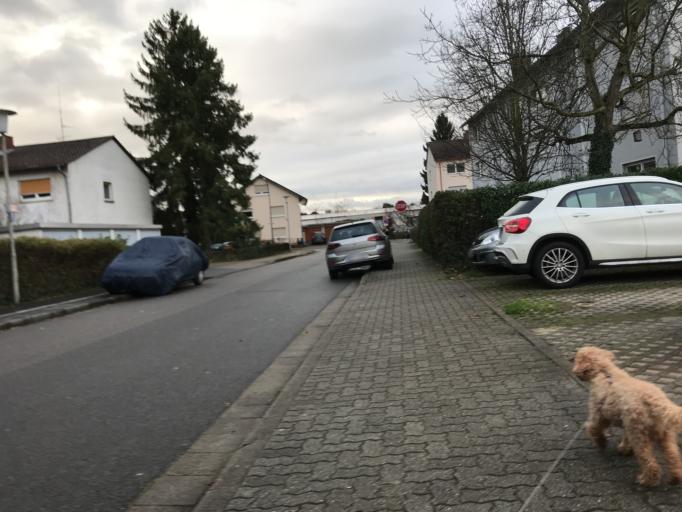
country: DE
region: Baden-Wuerttemberg
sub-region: Karlsruhe Region
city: Leimen
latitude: 49.3776
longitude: 8.6840
